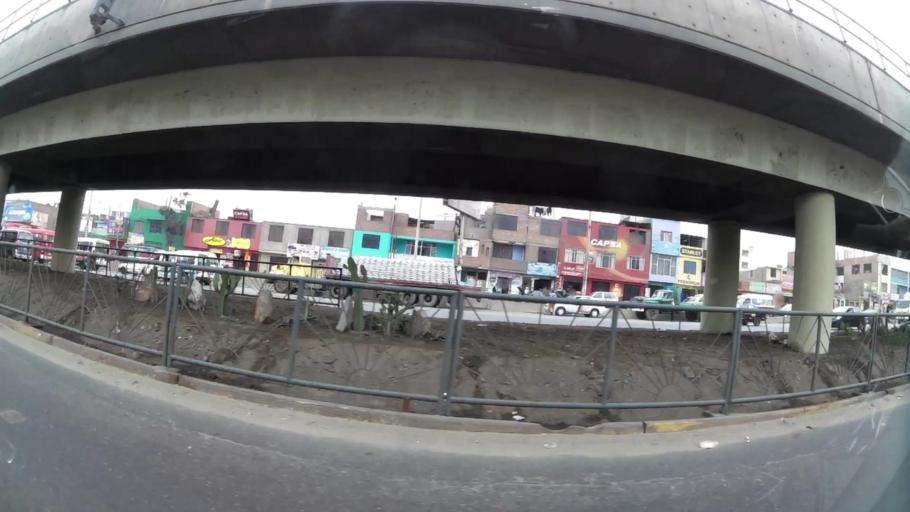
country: PE
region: Lima
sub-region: Lima
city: Surco
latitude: -12.1525
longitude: -76.9758
